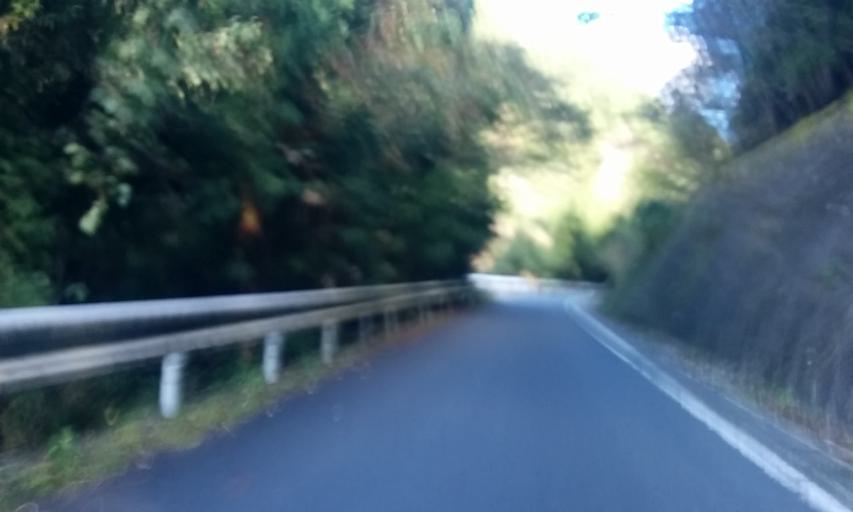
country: JP
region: Kyoto
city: Kameoka
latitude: 35.1301
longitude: 135.5714
